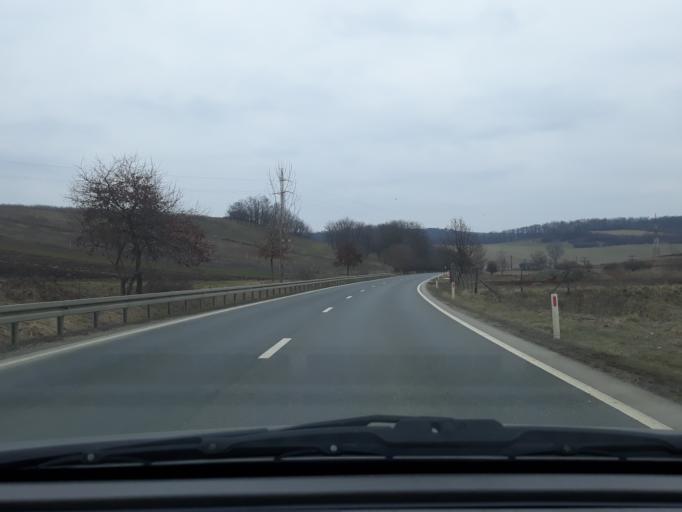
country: RO
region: Salaj
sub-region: Comuna Nusfalau
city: Nusfalau
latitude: 47.2207
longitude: 22.7399
